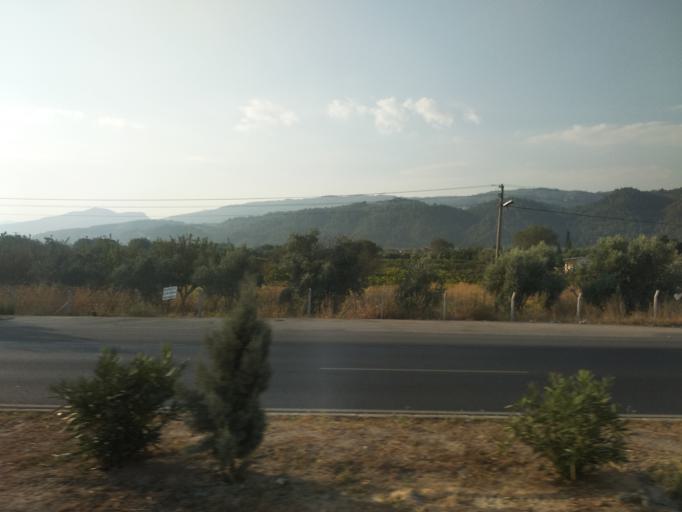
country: TR
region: Manisa
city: Ahmetli
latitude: 38.5025
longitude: 27.8751
